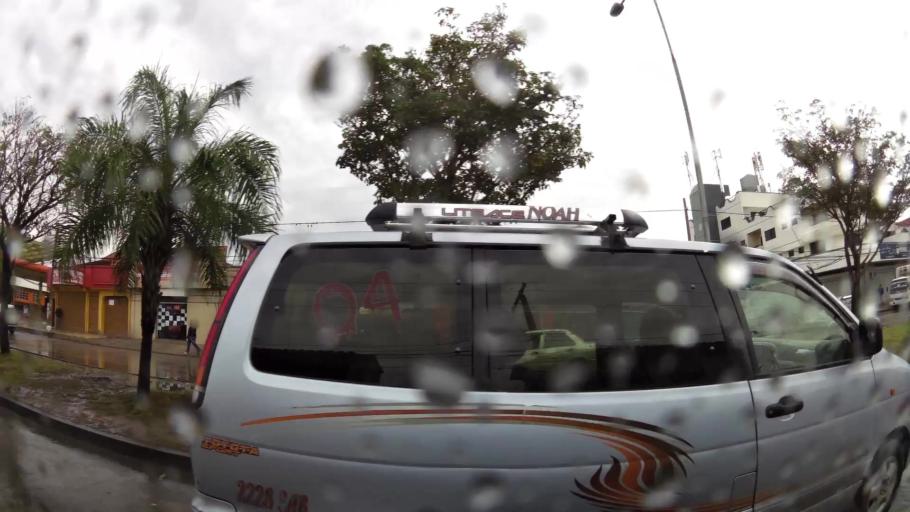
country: BO
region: Santa Cruz
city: Santa Cruz de la Sierra
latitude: -17.7681
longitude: -63.1527
